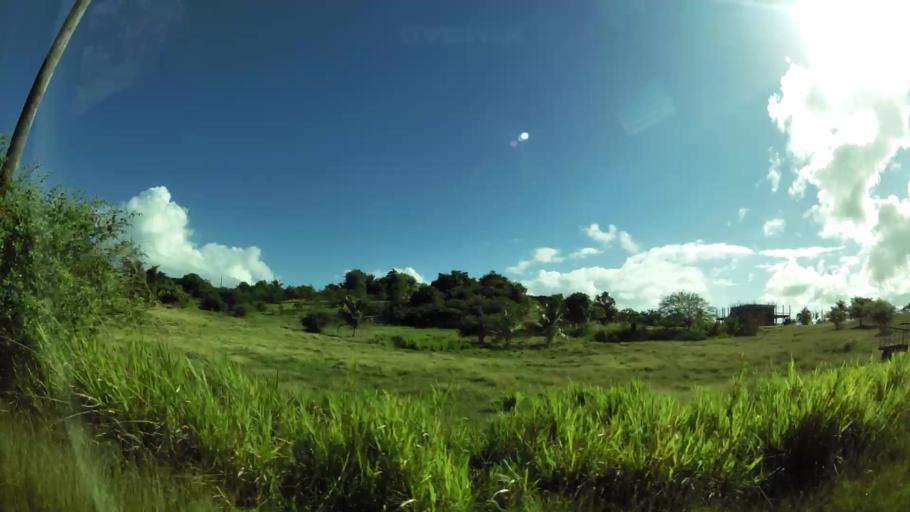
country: GP
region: Guadeloupe
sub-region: Guadeloupe
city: Petit-Canal
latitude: 16.3688
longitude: -61.4654
